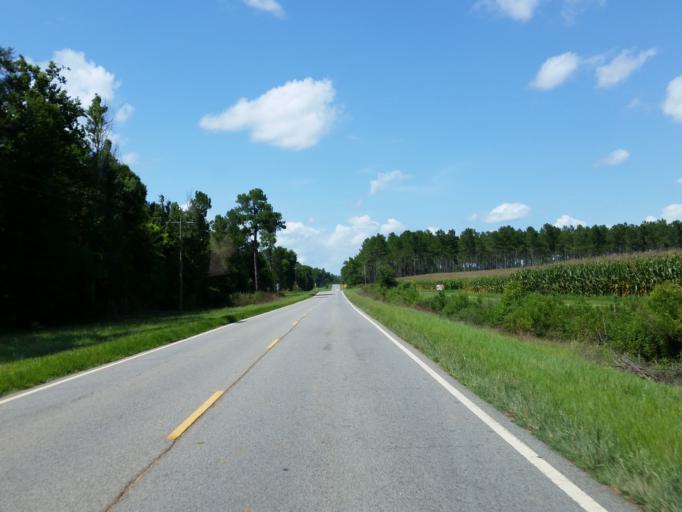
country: US
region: Georgia
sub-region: Tift County
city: Tifton
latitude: 31.5864
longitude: -83.4782
